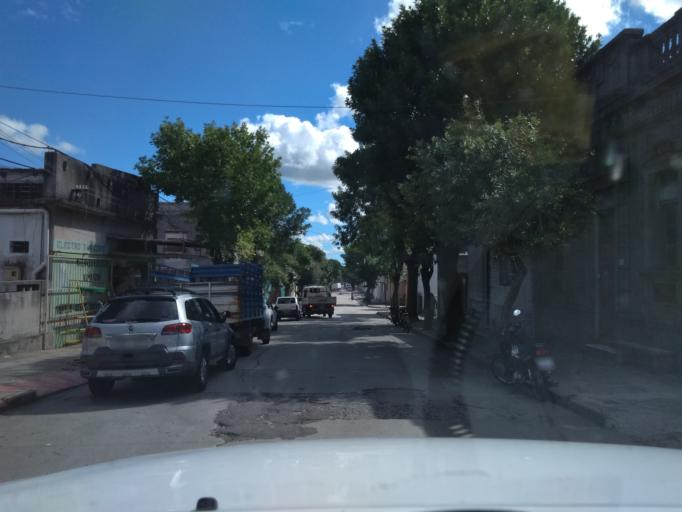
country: UY
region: Florida
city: Florida
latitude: -34.1018
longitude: -56.2151
